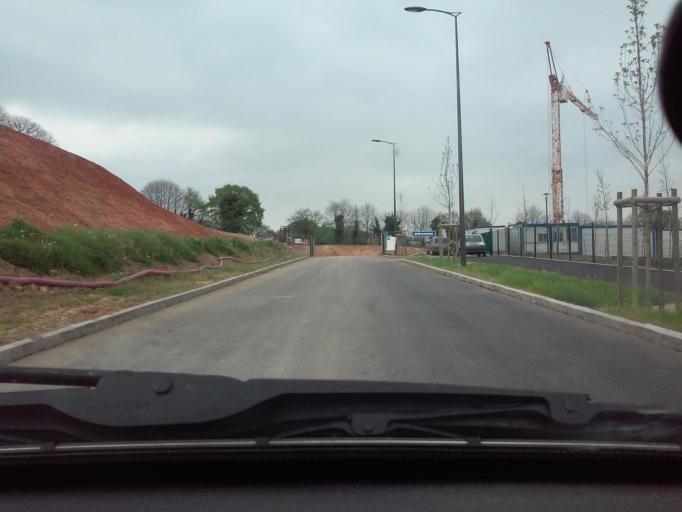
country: FR
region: Brittany
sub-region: Departement d'Ille-et-Vilaine
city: Fougeres
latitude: 48.3591
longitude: -1.1816
